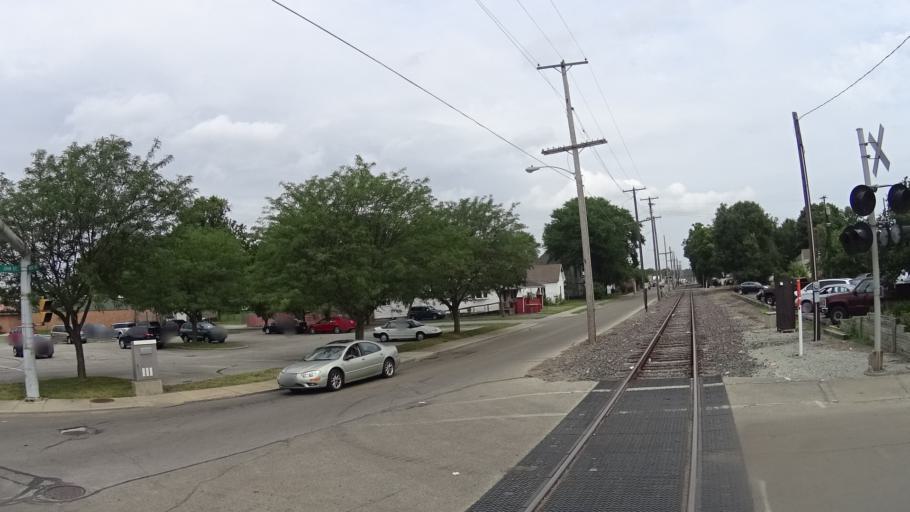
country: US
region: Indiana
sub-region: Madison County
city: Anderson
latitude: 40.1049
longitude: -85.6871
